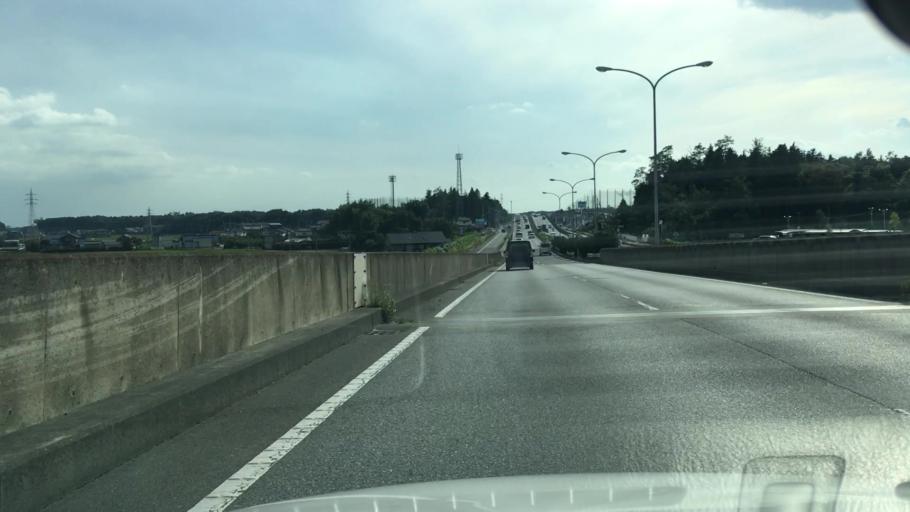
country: JP
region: Tochigi
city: Utsunomiya-shi
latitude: 36.5360
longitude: 139.9309
